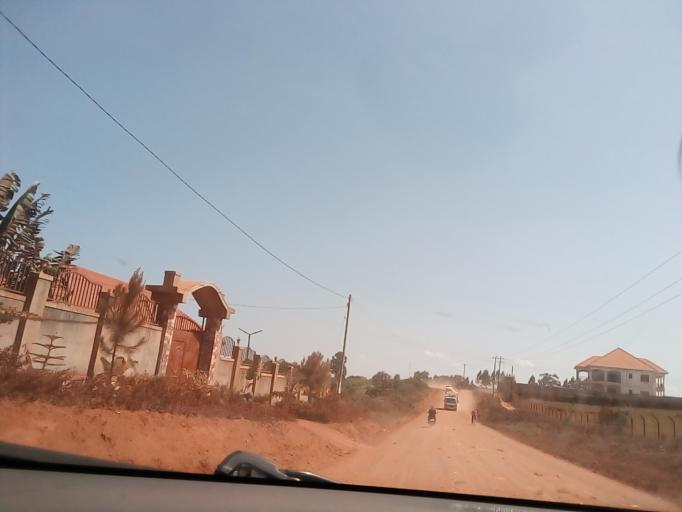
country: UG
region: Central Region
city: Masaka
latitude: -0.3635
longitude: 31.7485
